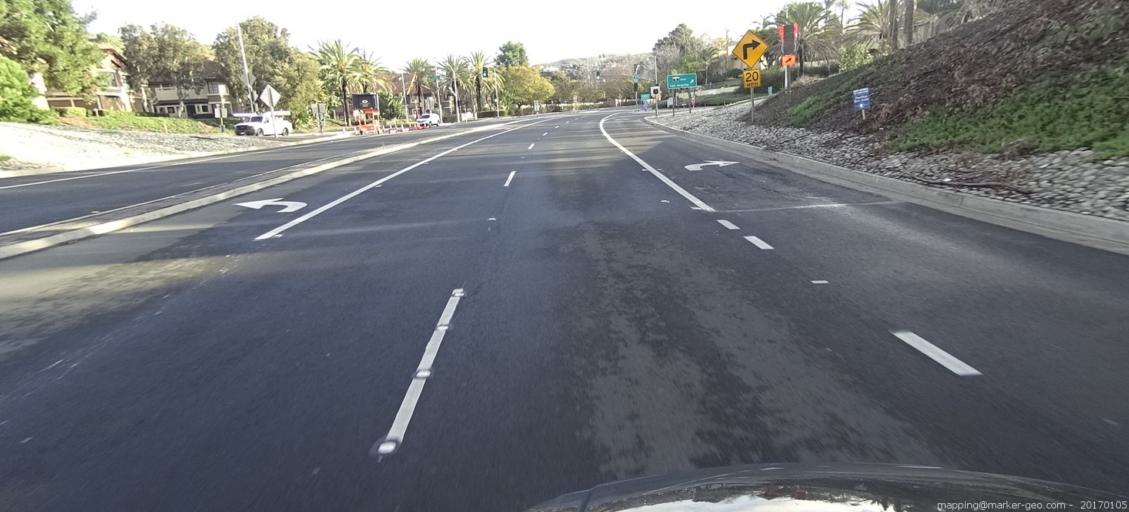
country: US
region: California
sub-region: Orange County
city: Dana Point
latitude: 33.4674
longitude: -117.6691
